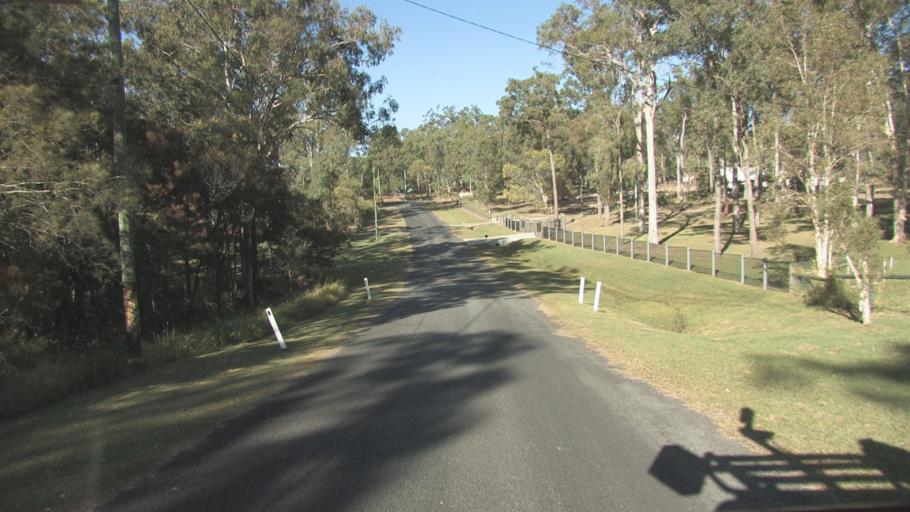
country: AU
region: Queensland
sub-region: Ipswich
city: Springfield Lakes
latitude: -27.6953
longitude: 152.9277
